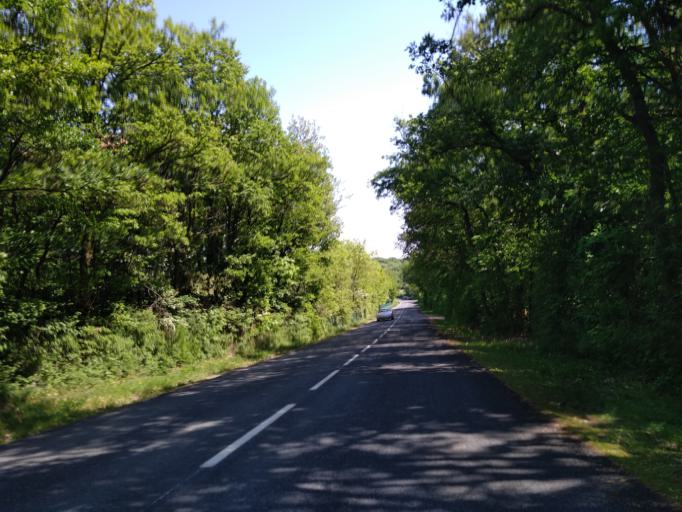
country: FR
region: Rhone-Alpes
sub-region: Departement du Rhone
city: Limonest
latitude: 45.8301
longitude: 4.8094
